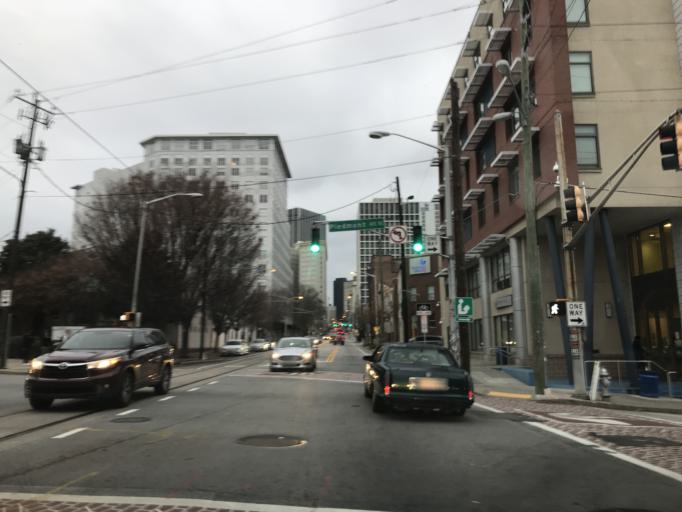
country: US
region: Georgia
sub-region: Fulton County
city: Atlanta
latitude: 33.7545
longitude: -84.3821
